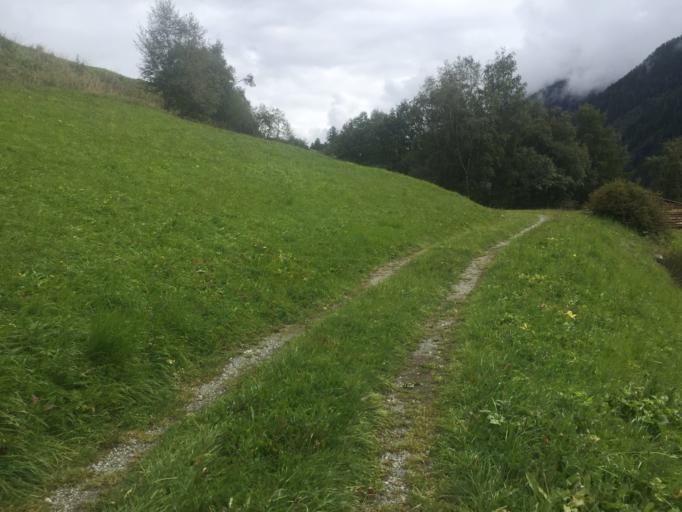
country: CH
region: Grisons
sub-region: Inn District
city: Zernez
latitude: 46.7731
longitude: 10.1340
